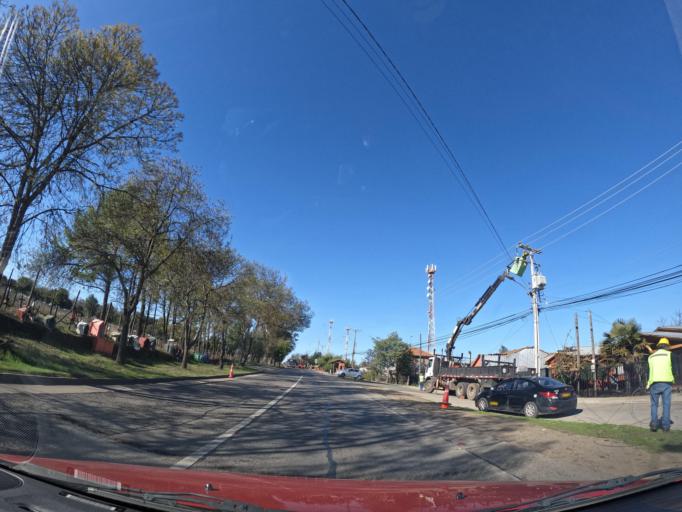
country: CL
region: Maule
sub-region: Provincia de Cauquenes
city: Cauquenes
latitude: -35.9571
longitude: -72.3047
